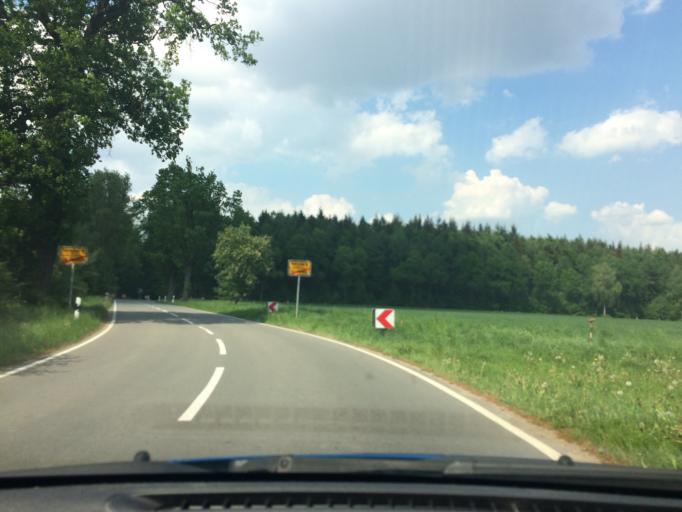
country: DE
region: Lower Saxony
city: Tosterglope
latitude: 53.1975
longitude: 10.7974
